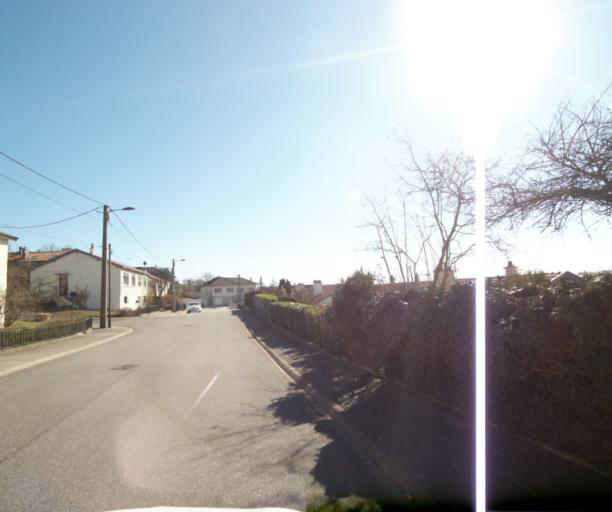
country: FR
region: Lorraine
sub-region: Departement de Meurthe-et-Moselle
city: Essey-les-Nancy
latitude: 48.7113
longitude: 6.2213
